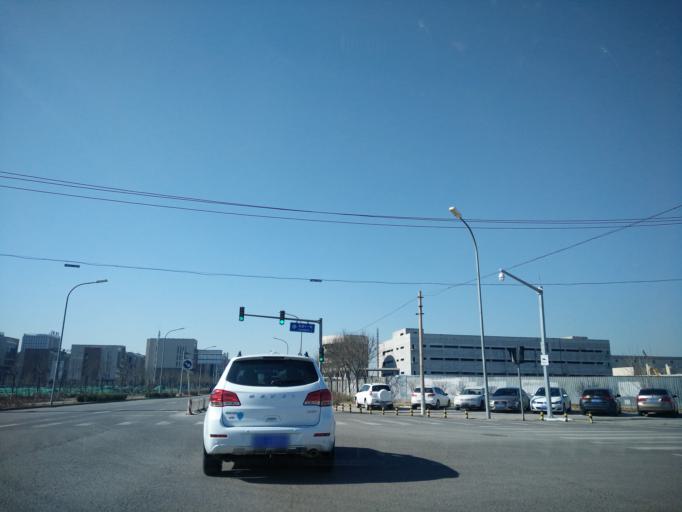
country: CN
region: Beijing
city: Taihu
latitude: 39.7848
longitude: 116.5512
